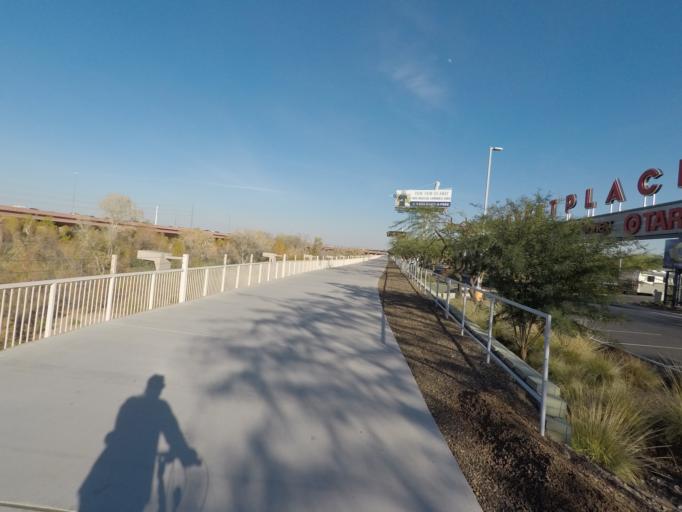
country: US
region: Arizona
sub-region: Maricopa County
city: Tempe
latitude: 33.4345
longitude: -111.9051
